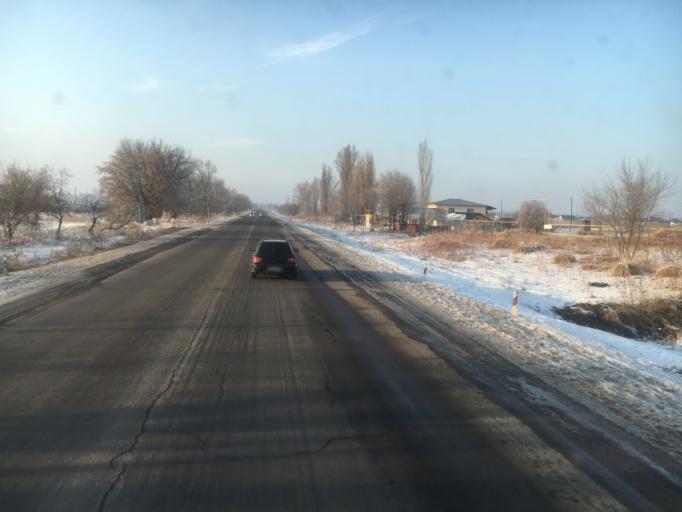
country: KZ
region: Almaty Oblysy
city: Burunday
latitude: 43.3422
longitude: 76.6575
